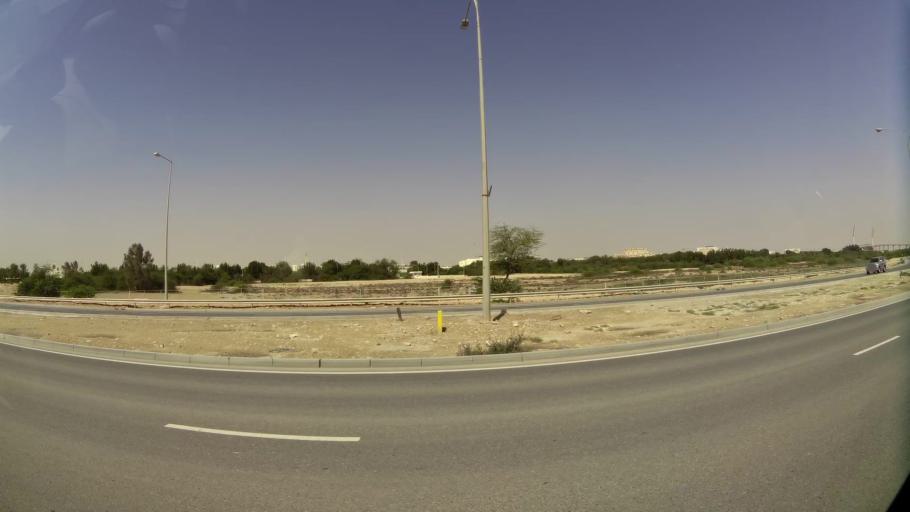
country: QA
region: Baladiyat ad Dawhah
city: Doha
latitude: 25.3682
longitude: 51.4976
